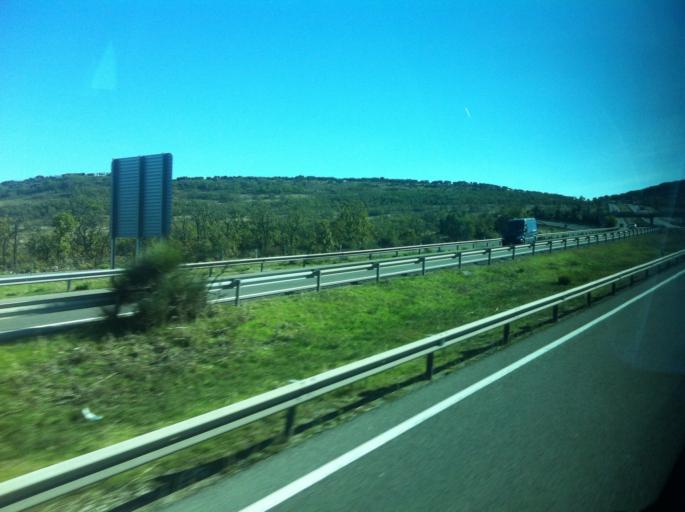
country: ES
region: Madrid
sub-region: Provincia de Madrid
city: Buitrago del Lozoya
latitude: 40.9678
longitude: -3.6411
